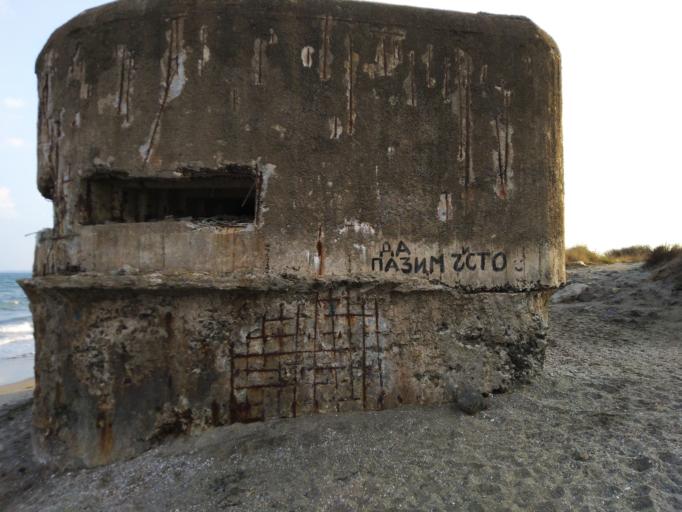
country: BG
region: Burgas
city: Aheloy
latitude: 42.6240
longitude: 27.6346
